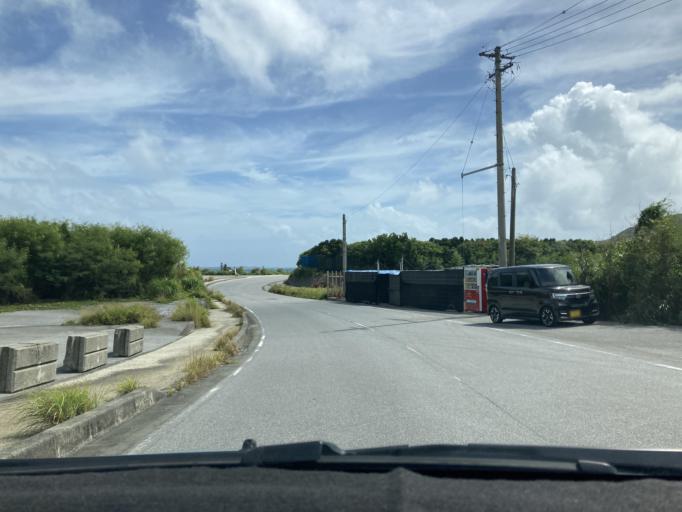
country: JP
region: Okinawa
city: Ginowan
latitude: 26.1871
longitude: 127.8211
